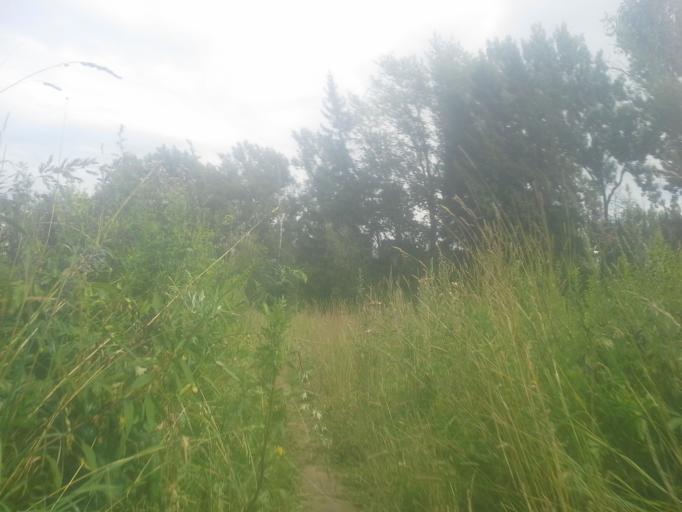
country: RU
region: Moskovskaya
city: Zhavoronki
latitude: 55.6448
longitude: 37.1312
